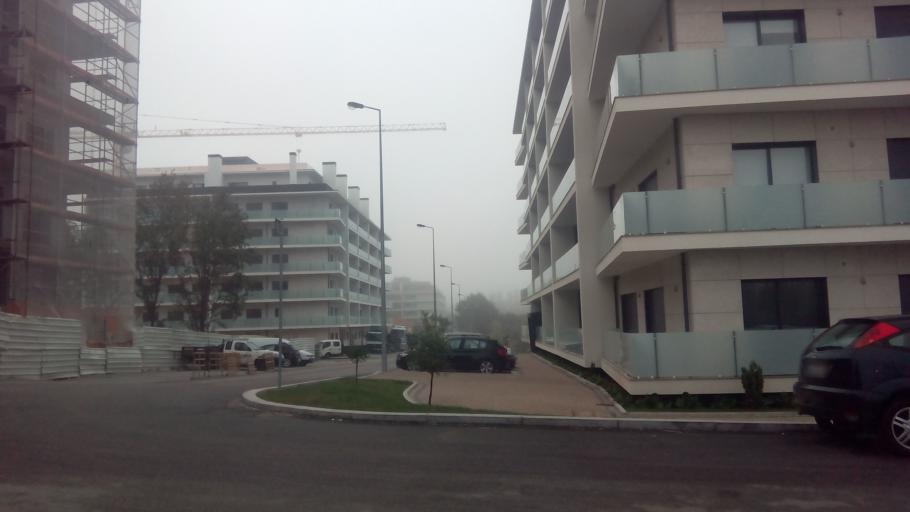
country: PT
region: Porto
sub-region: Paredes
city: Paredes
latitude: 41.2087
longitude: -8.3234
